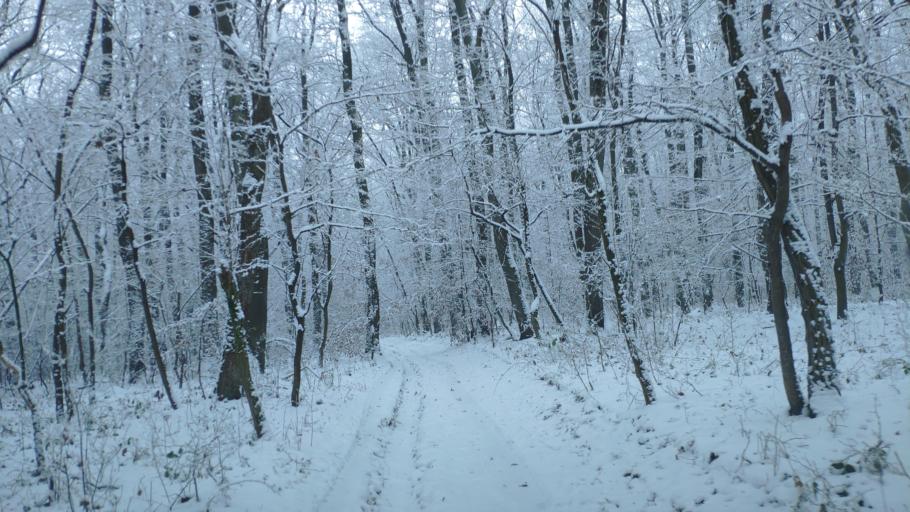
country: SK
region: Kosicky
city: Kosice
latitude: 48.6451
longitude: 21.1821
